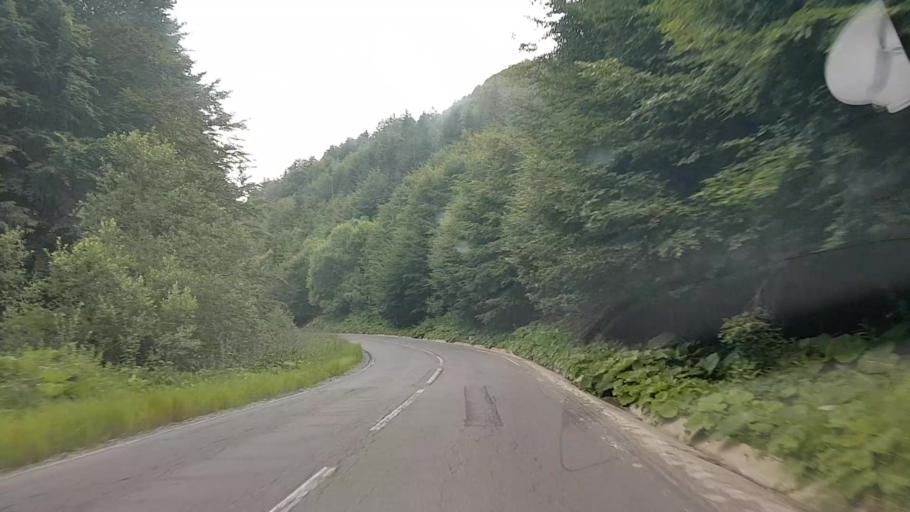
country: RO
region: Harghita
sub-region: Comuna Praid
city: Ocna de Sus
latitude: 46.6228
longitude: 25.2523
